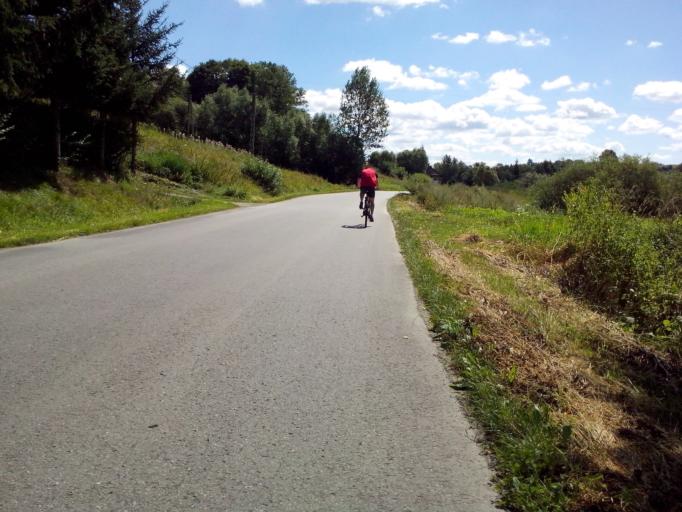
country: PL
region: Subcarpathian Voivodeship
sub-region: Powiat brzozowski
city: Domaradz
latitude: 49.7908
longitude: 21.9782
